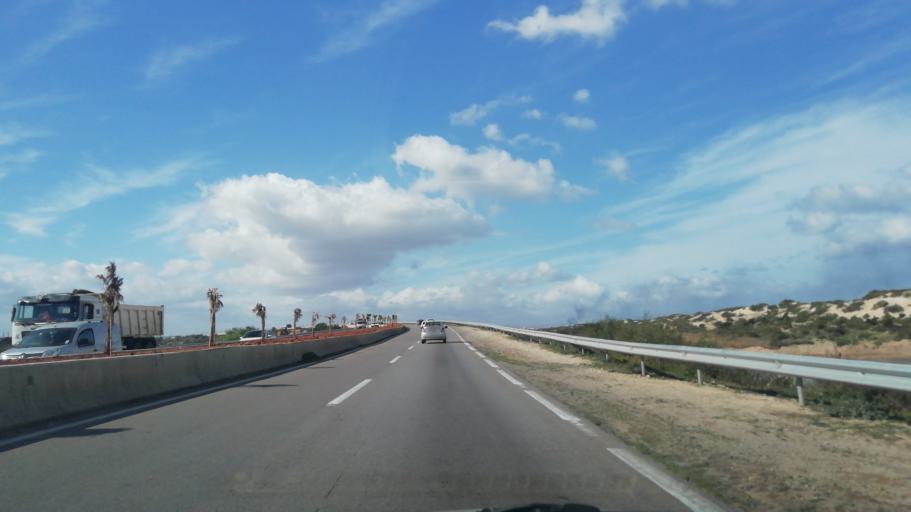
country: DZ
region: Oran
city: Ain el Bya
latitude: 35.7859
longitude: -0.1234
